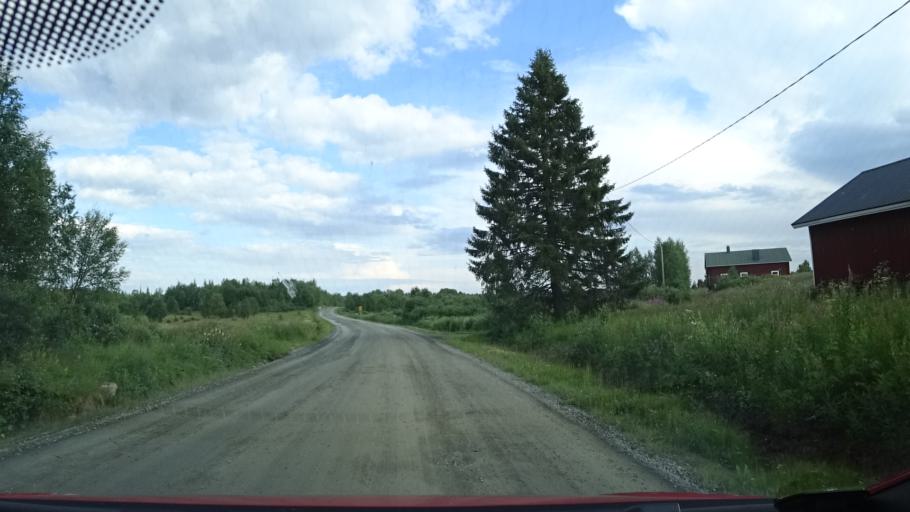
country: FI
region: Lapland
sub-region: Tunturi-Lappi
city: Kittilae
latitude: 67.9247
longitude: 25.0510
